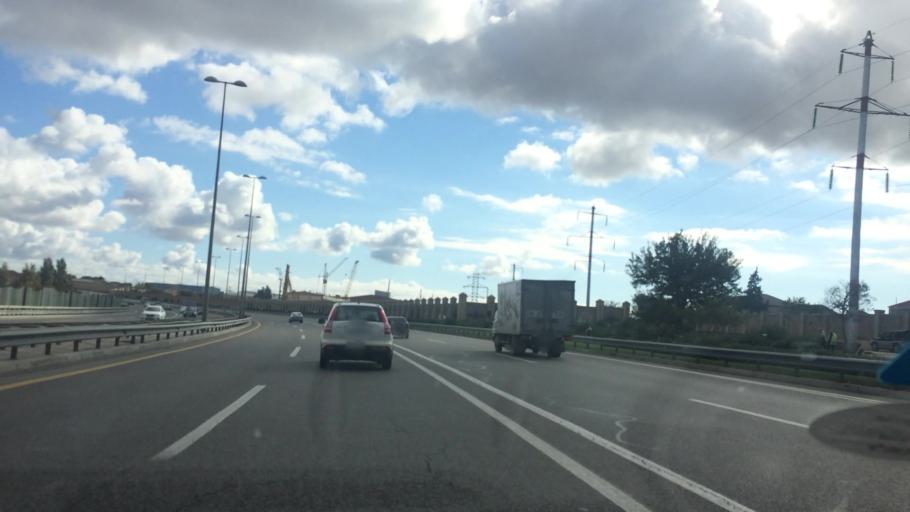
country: AZ
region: Baki
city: Ramana
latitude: 40.4387
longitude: 49.9756
